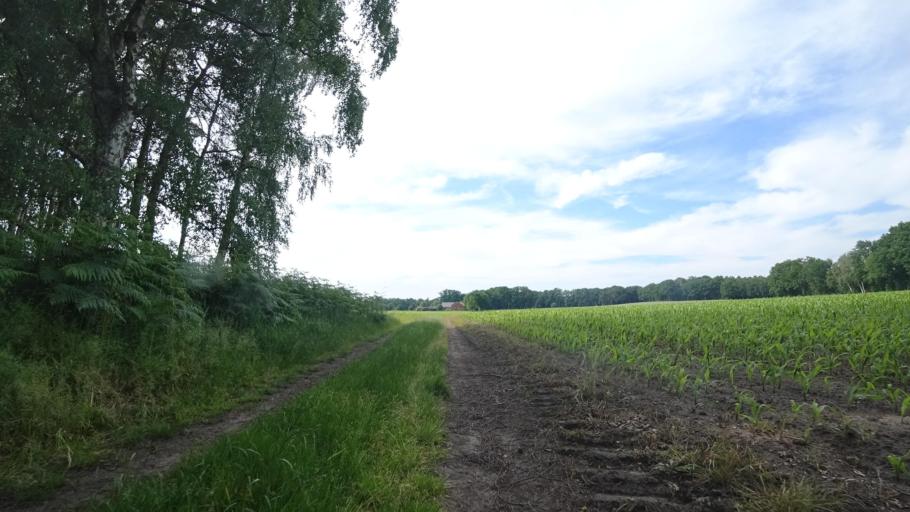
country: DE
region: North Rhine-Westphalia
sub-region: Regierungsbezirk Detmold
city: Verl
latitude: 51.9009
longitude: 8.4609
